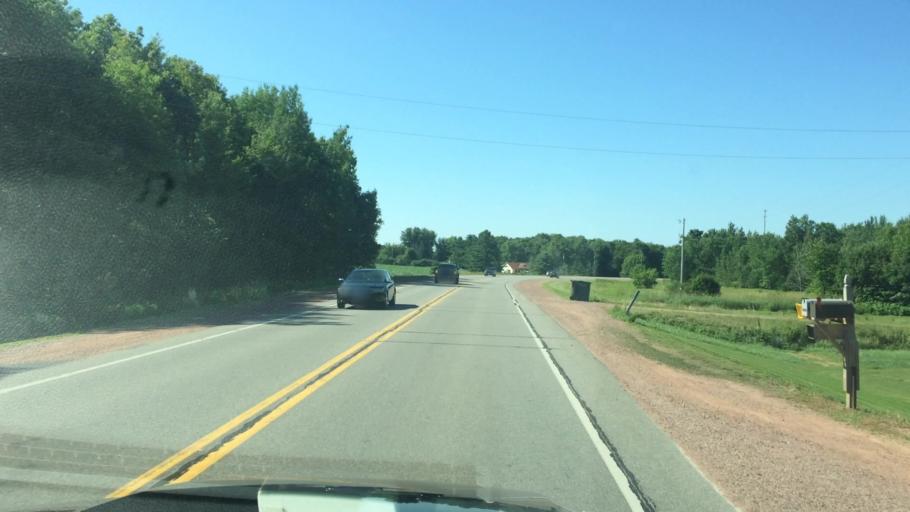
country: US
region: Wisconsin
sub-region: Marathon County
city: Stratford
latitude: 44.7391
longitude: -90.0794
